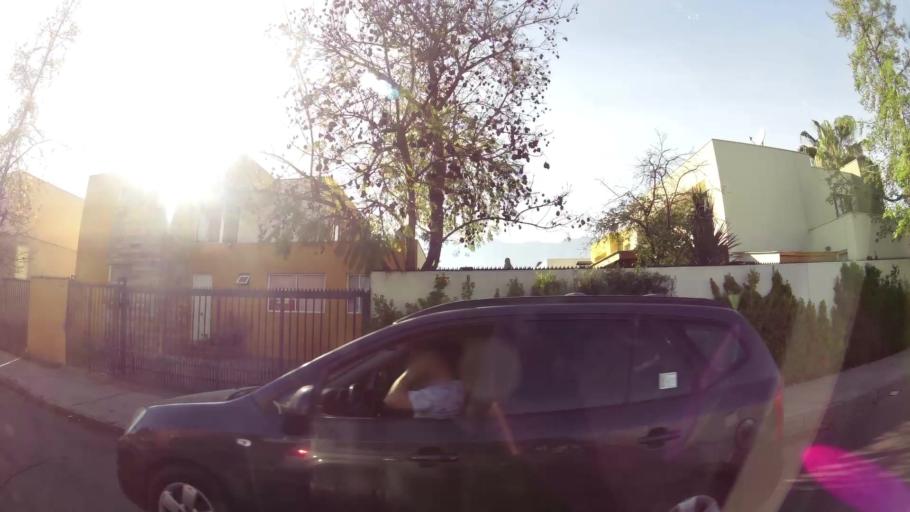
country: CL
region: Santiago Metropolitan
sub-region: Provincia de Santiago
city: Villa Presidente Frei, Nunoa, Santiago, Chile
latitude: -33.4844
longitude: -70.5554
